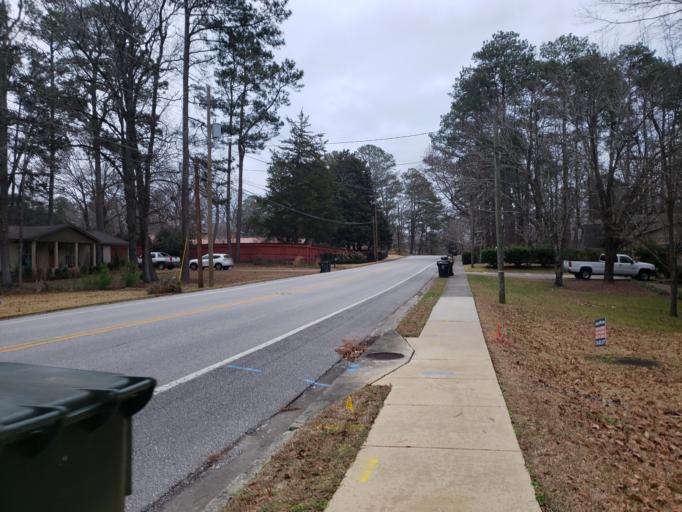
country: US
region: Alabama
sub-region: Lee County
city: Auburn
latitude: 32.5989
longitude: -85.4576
